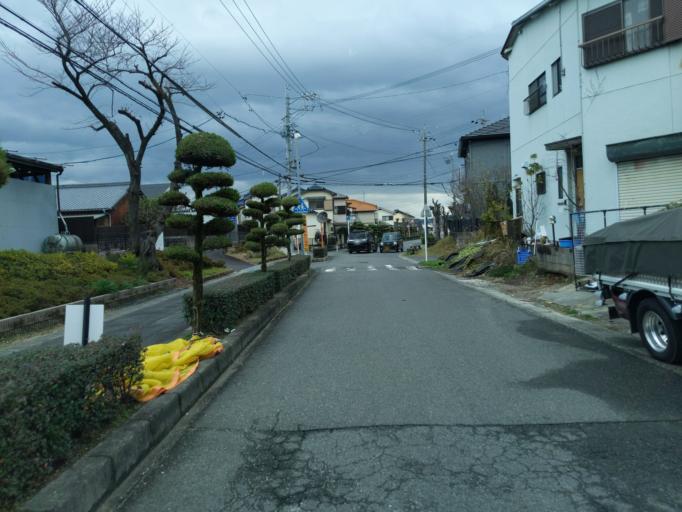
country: JP
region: Aichi
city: Kasugai
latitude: 35.2583
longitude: 136.9876
